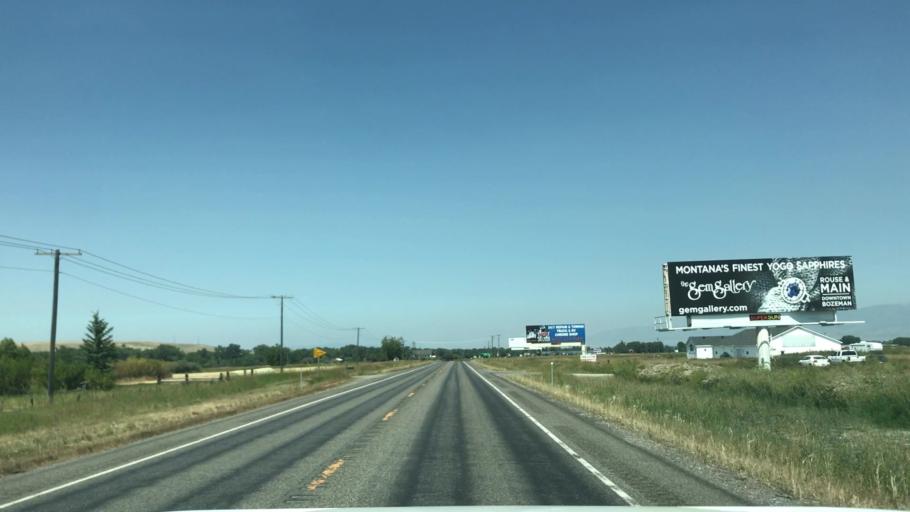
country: US
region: Montana
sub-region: Gallatin County
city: Four Corners
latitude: 45.6345
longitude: -111.1969
